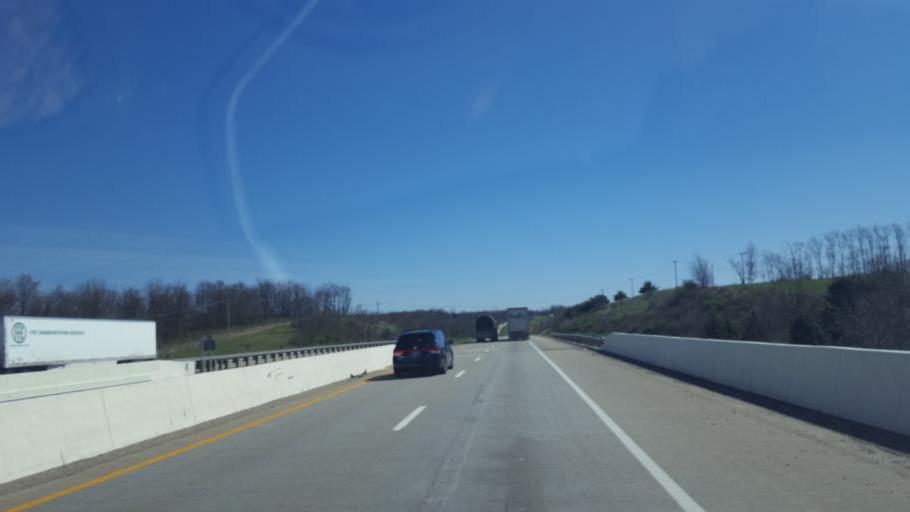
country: US
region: Ohio
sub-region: Belmont County
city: Bethesda
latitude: 40.0598
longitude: -81.0532
